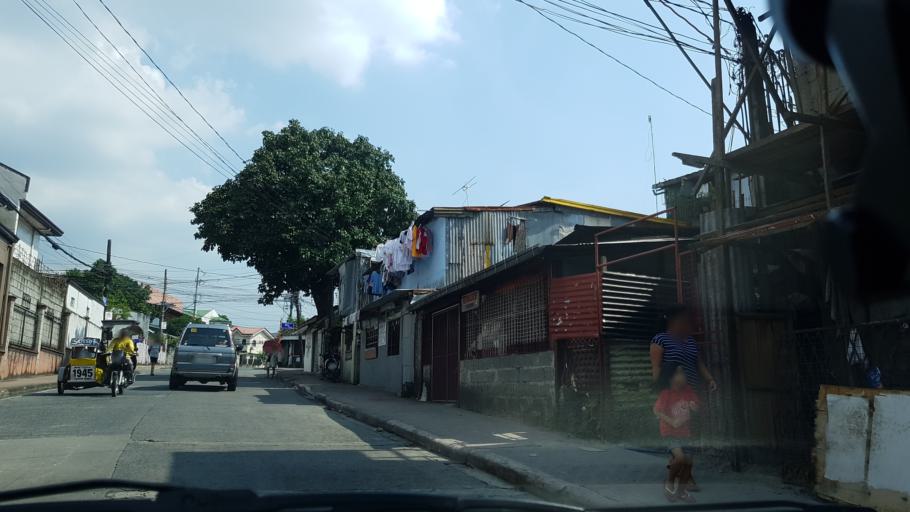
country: PH
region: Calabarzon
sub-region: Province of Rizal
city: Antipolo
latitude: 14.6559
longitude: 121.1153
